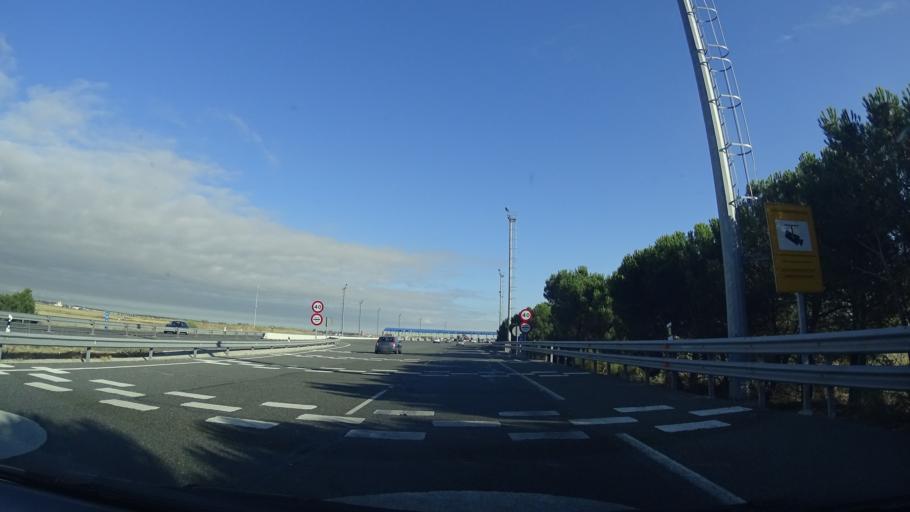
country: ES
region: Castille and Leon
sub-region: Provincia de Avila
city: Sanchidrian
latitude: 40.8808
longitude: -4.5697
